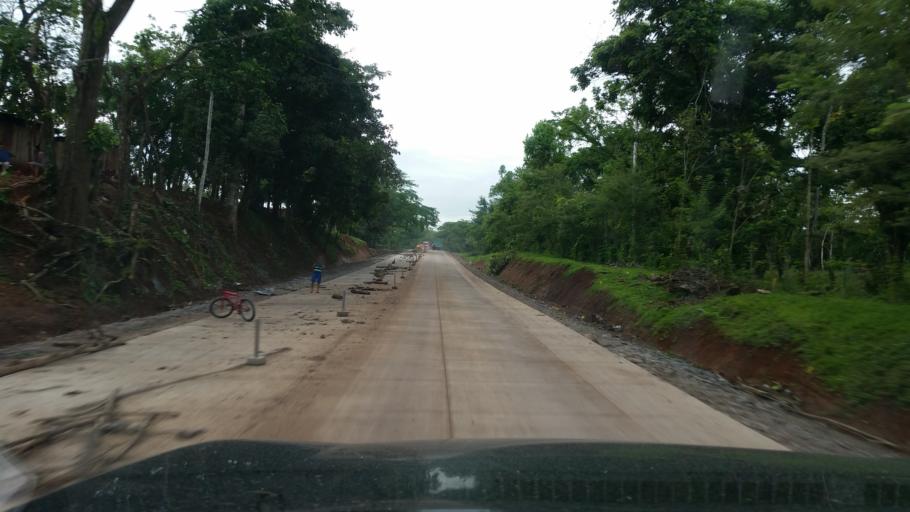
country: NI
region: Matagalpa
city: Rio Blanco
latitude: 13.2034
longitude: -84.9487
